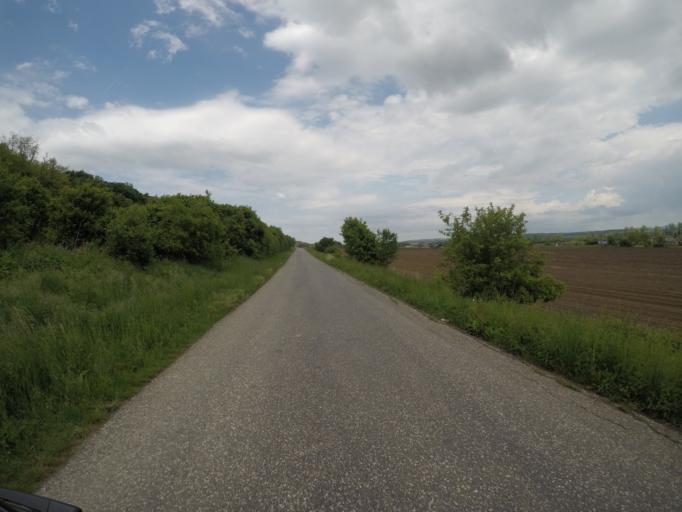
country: SK
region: Banskobystricky
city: Dudince
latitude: 48.1126
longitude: 18.8727
